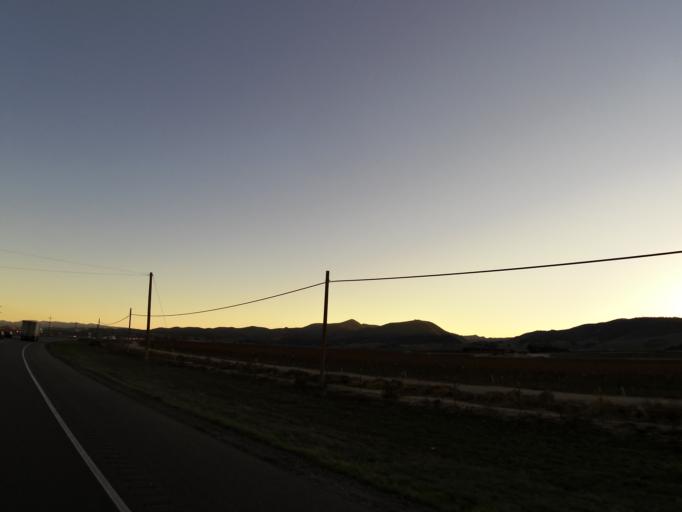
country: US
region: California
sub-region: Monterey County
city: King City
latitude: 36.2535
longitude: -121.1773
